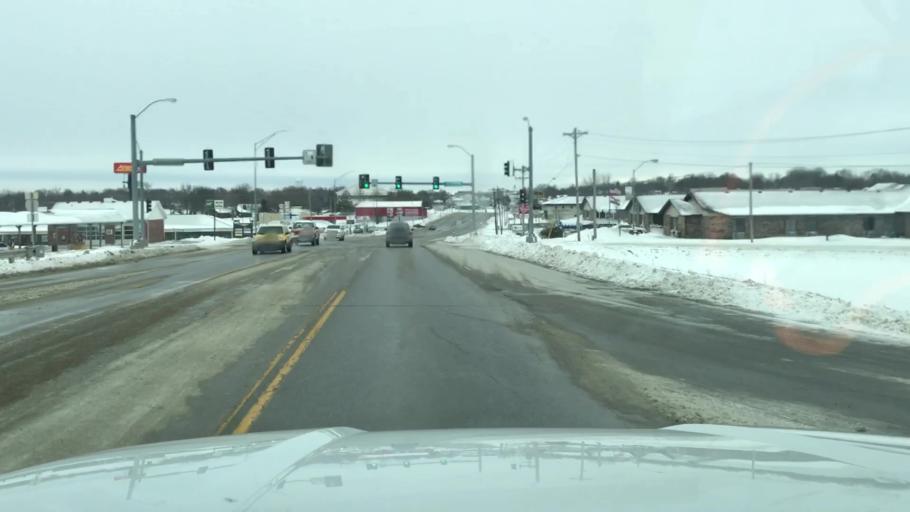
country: US
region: Missouri
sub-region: Clinton County
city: Cameron
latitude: 39.7535
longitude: -94.2343
